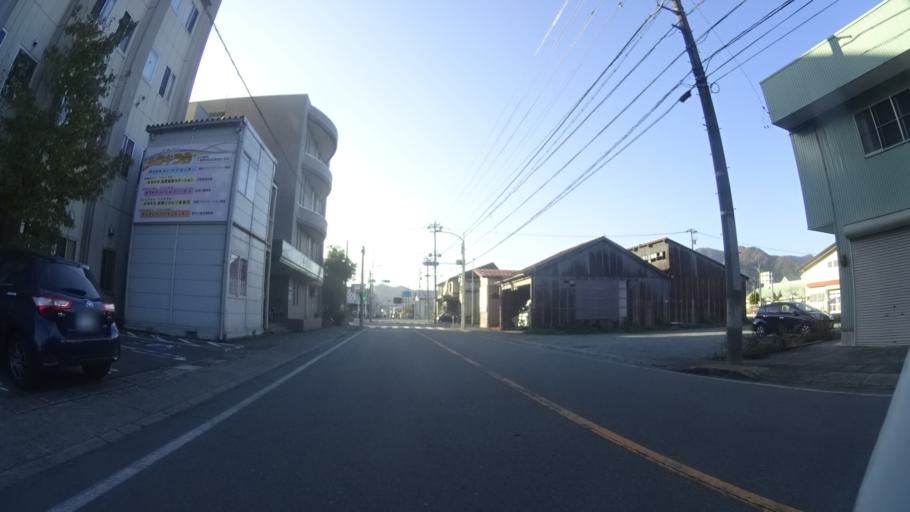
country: JP
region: Fukui
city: Ono
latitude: 35.9905
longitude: 136.4894
